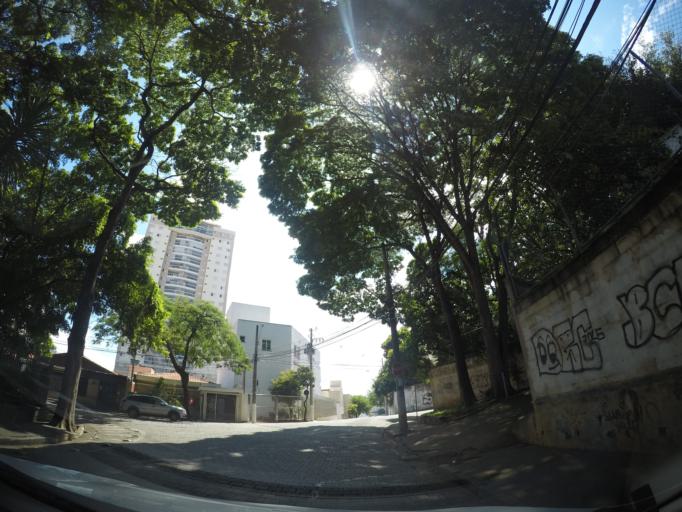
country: BR
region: Sao Paulo
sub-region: Guarulhos
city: Guarulhos
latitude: -23.4623
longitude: -46.5349
